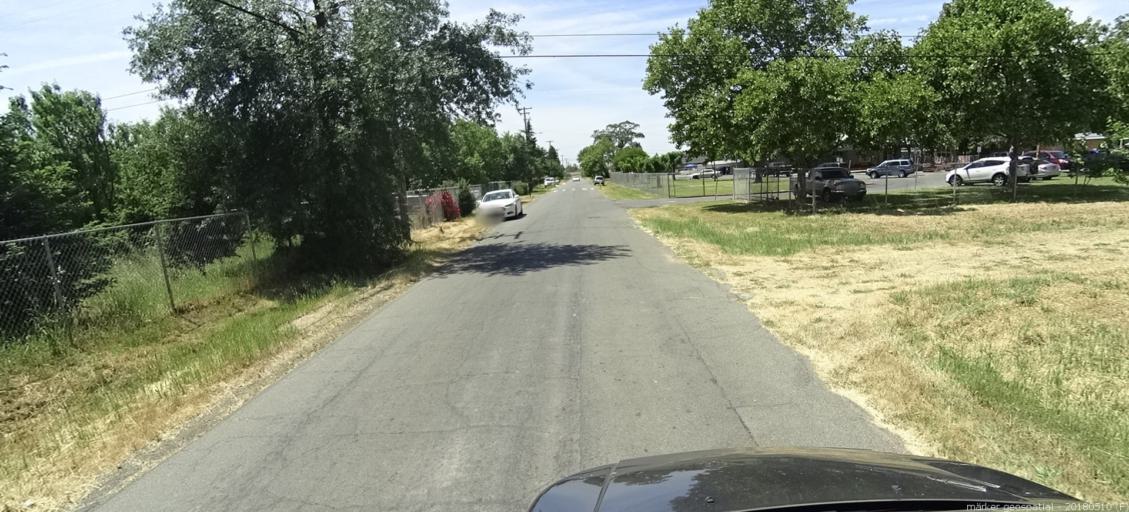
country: US
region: California
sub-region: Sacramento County
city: Rio Linda
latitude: 38.6348
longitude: -121.4636
